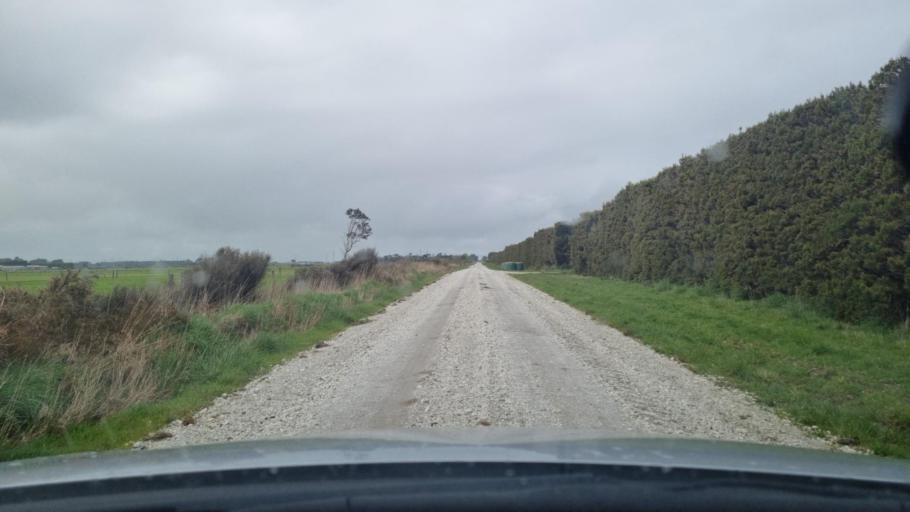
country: NZ
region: Southland
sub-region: Invercargill City
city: Invercargill
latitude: -46.4996
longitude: 168.4115
